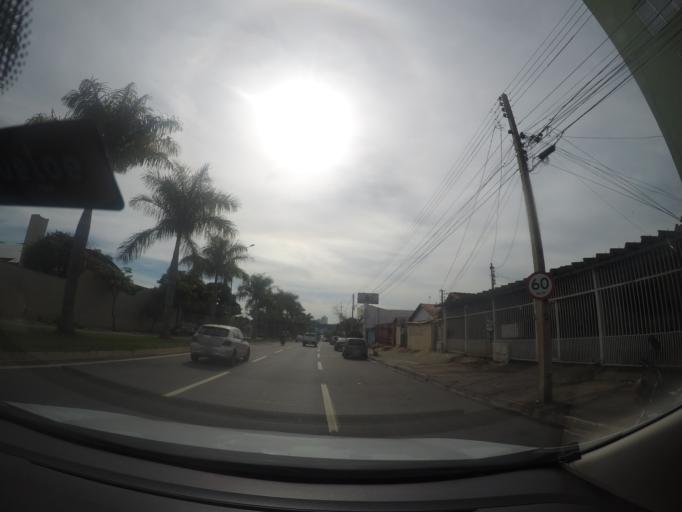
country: BR
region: Goias
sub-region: Goiania
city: Goiania
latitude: -16.6648
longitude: -49.2730
